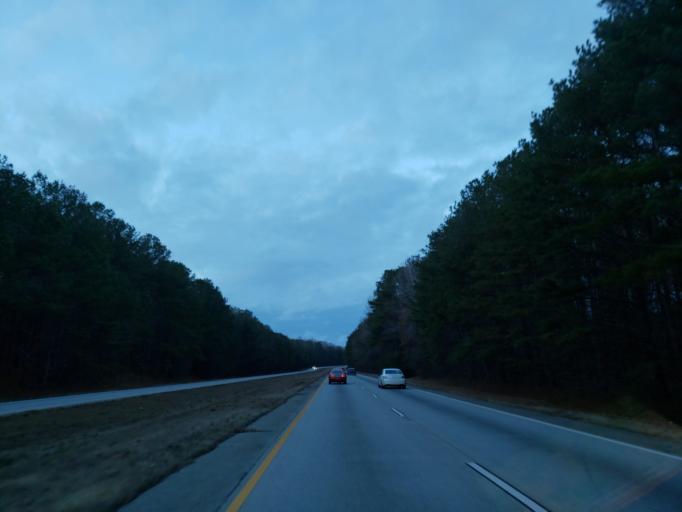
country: US
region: Georgia
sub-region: Fulton County
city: Union City
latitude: 33.6898
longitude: -84.5739
